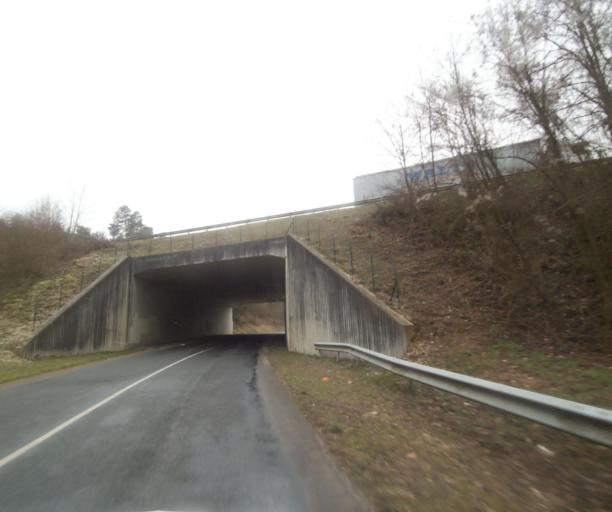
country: FR
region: Champagne-Ardenne
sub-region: Departement de la Haute-Marne
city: Chevillon
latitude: 48.5228
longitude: 5.0892
